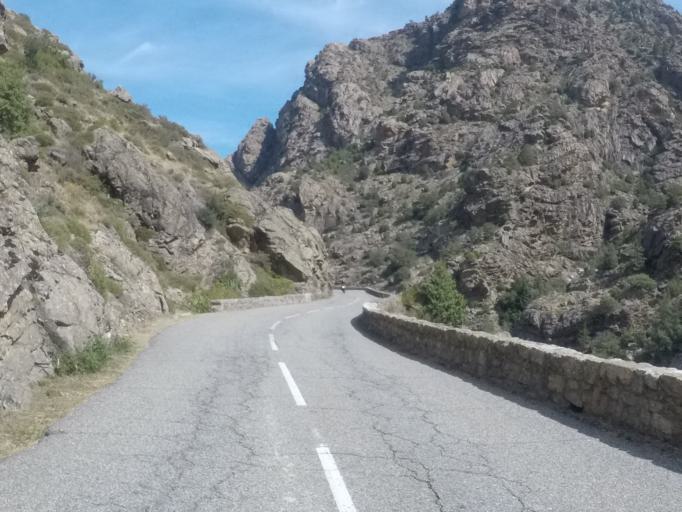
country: FR
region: Corsica
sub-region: Departement de la Haute-Corse
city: Corte
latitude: 42.3609
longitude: 9.0656
